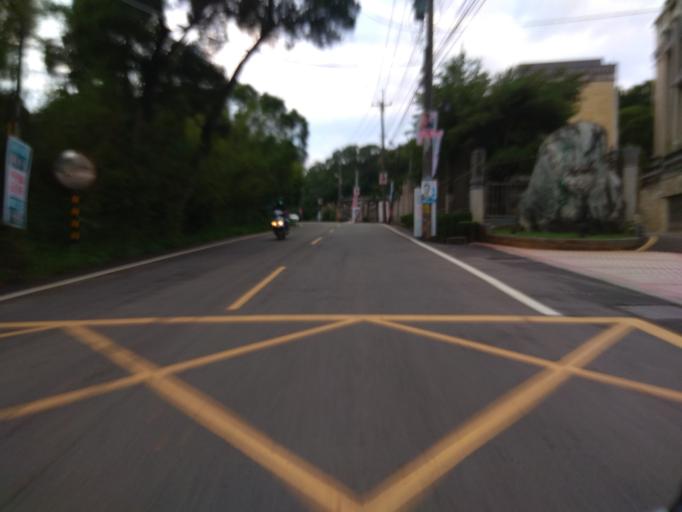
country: TW
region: Taiwan
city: Daxi
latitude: 24.9435
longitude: 121.1867
